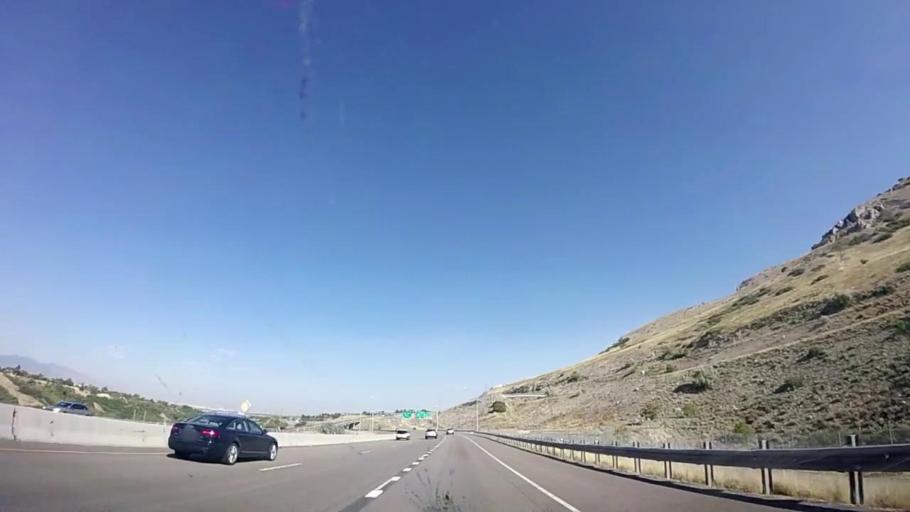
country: US
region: Utah
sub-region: Salt Lake County
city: East Millcreek
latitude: 40.7098
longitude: -111.7998
